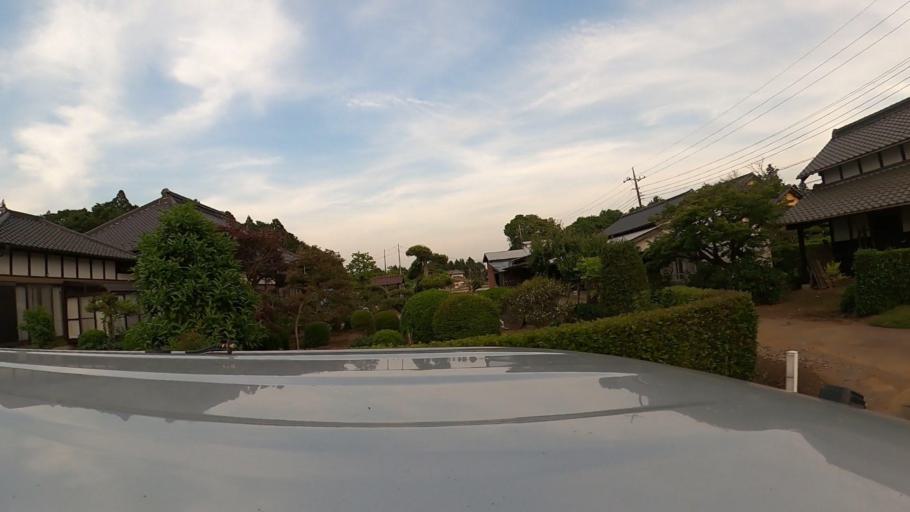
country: JP
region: Ibaraki
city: Ushiku
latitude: 36.0087
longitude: 140.1223
